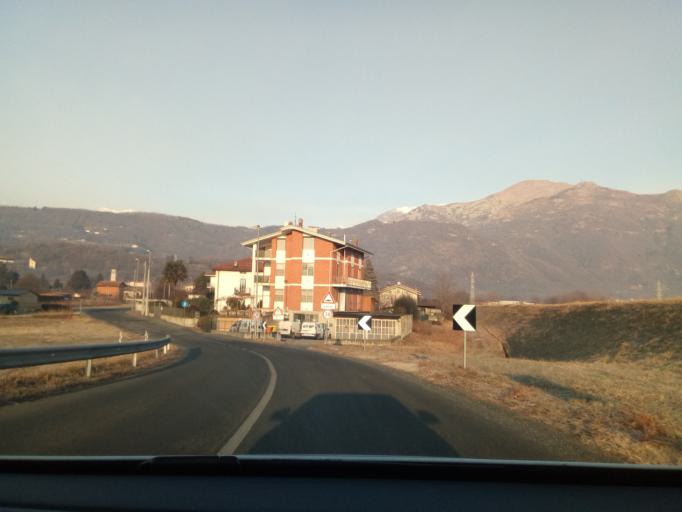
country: IT
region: Piedmont
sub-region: Provincia di Torino
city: Fiorano Canavese
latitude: 45.4670
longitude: 7.8417
